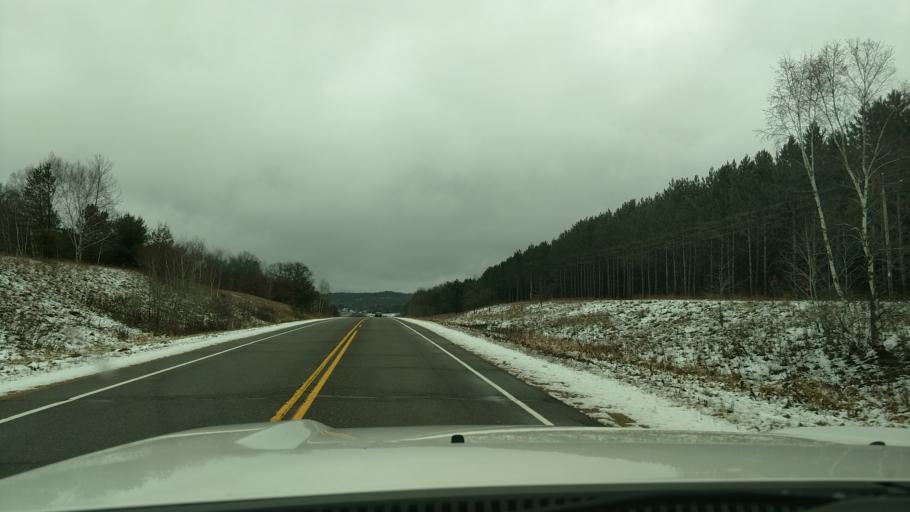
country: US
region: Wisconsin
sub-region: Dunn County
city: Tainter Lake
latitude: 45.1241
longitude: -91.8689
